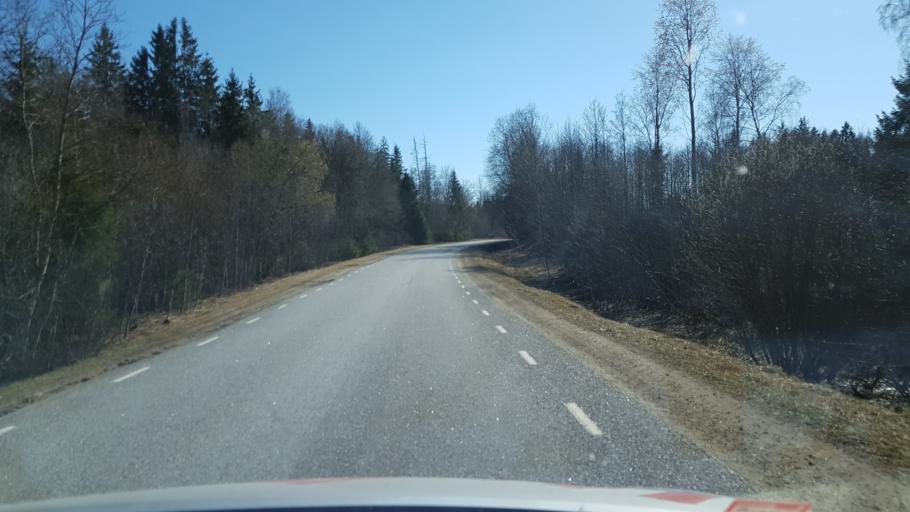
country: EE
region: Laeaene-Virumaa
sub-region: Tamsalu vald
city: Tamsalu
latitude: 59.0576
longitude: 26.1018
